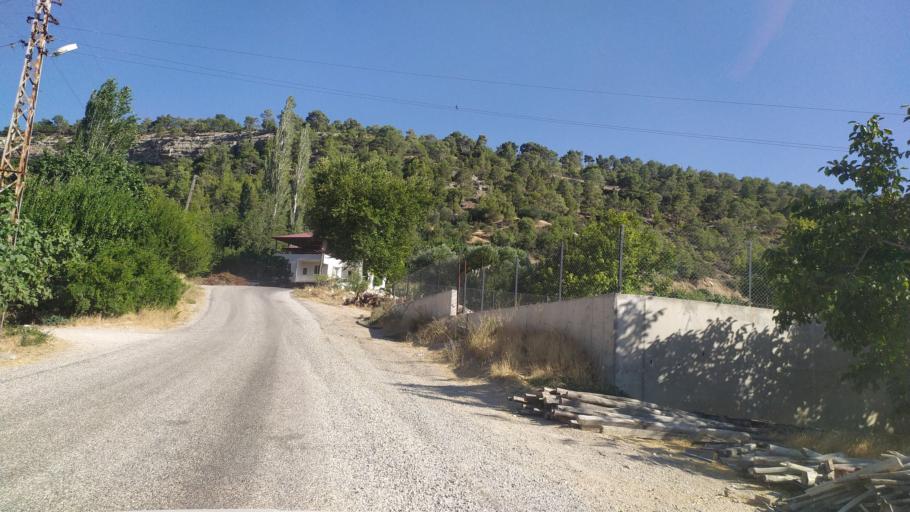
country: TR
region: Mersin
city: Mut
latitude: 36.7059
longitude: 33.4736
